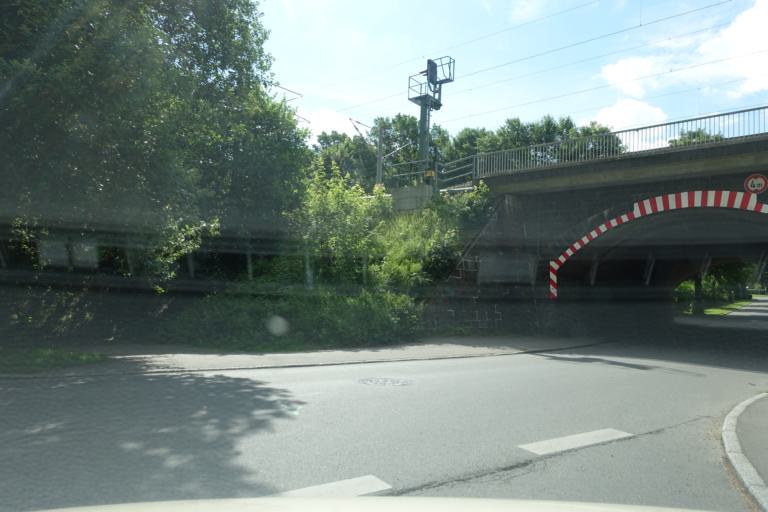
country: DE
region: Saxony
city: Oederan
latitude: 50.8579
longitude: 13.1809
